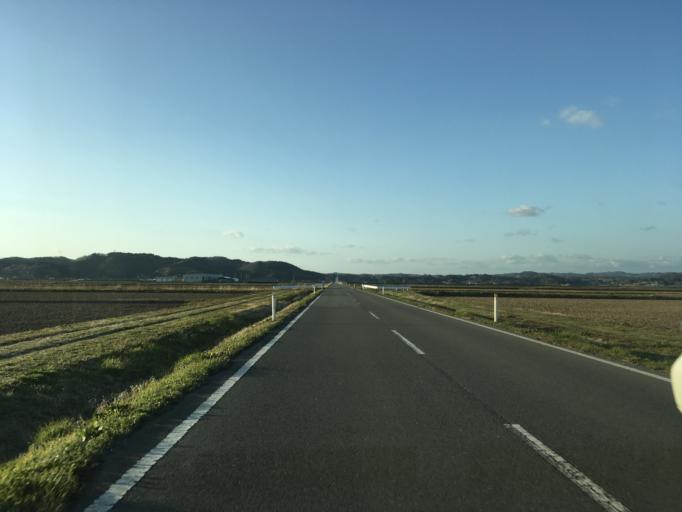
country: JP
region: Iwate
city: Ichinoseki
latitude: 38.7324
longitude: 141.2392
